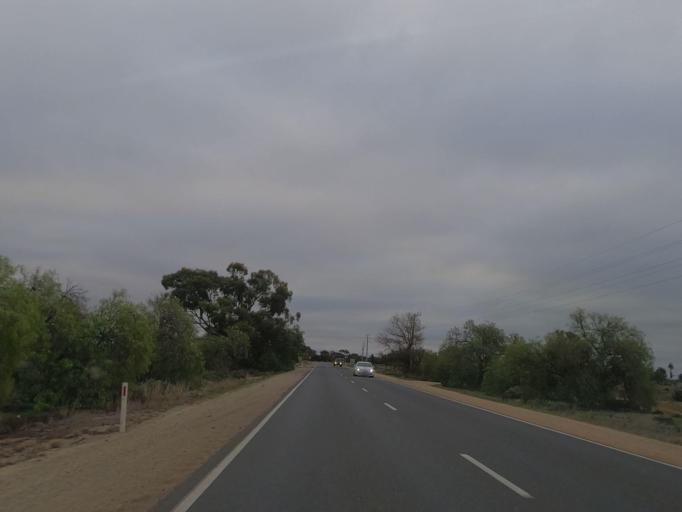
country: AU
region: Victoria
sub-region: Swan Hill
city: Swan Hill
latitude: -35.4439
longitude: 143.6178
